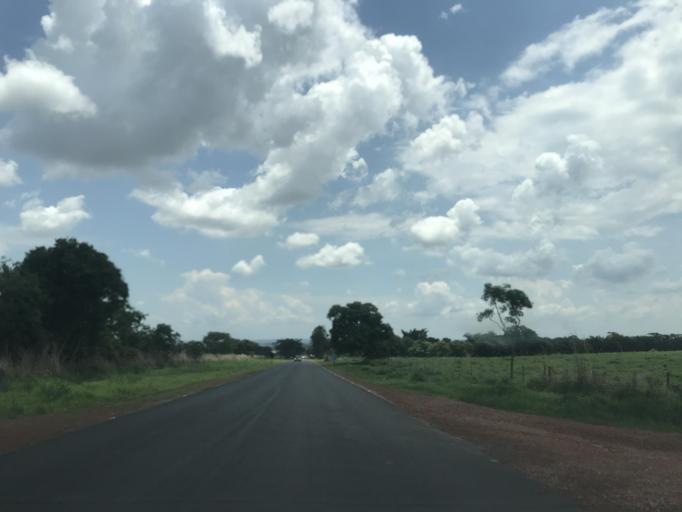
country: BR
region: Goias
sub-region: Bela Vista De Goias
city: Bela Vista de Goias
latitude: -17.0400
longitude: -48.6629
